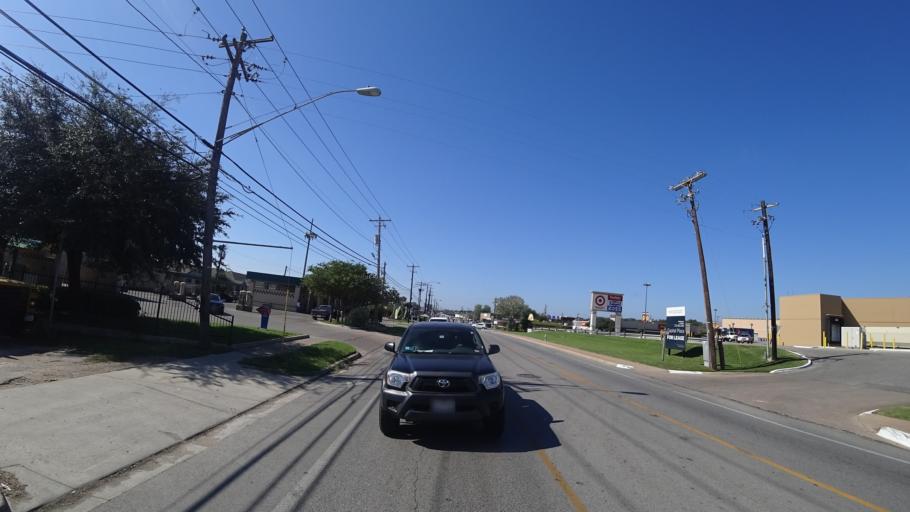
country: US
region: Texas
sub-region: Travis County
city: Austin
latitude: 30.3125
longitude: -97.7056
